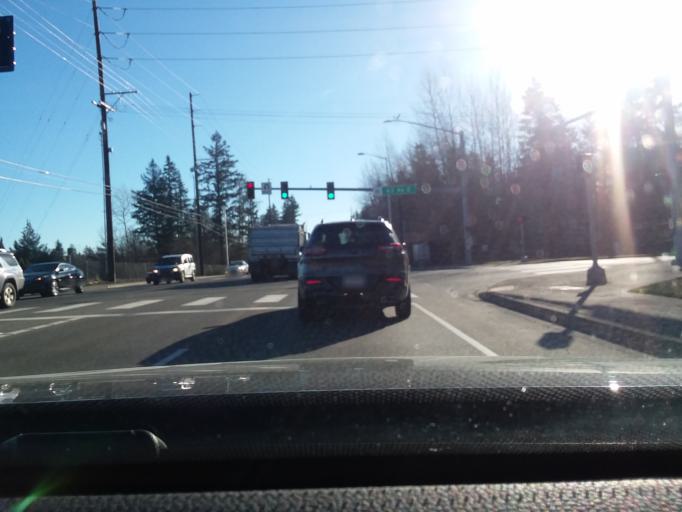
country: US
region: Washington
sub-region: Pierce County
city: Frederickson
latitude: 47.0965
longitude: -122.3460
